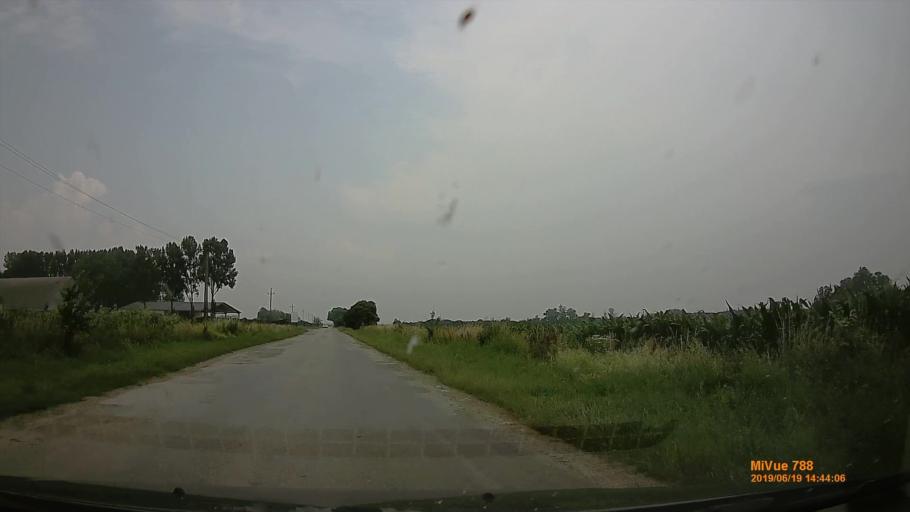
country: HU
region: Baranya
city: Szigetvar
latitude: 46.0320
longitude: 17.8251
